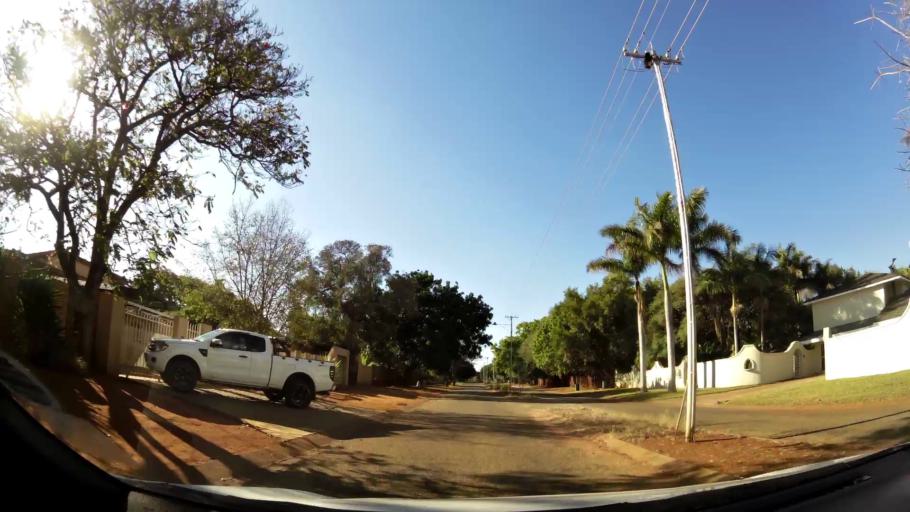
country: ZA
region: Limpopo
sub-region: Waterberg District Municipality
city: Mokopane
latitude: -24.2040
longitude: 29.0076
